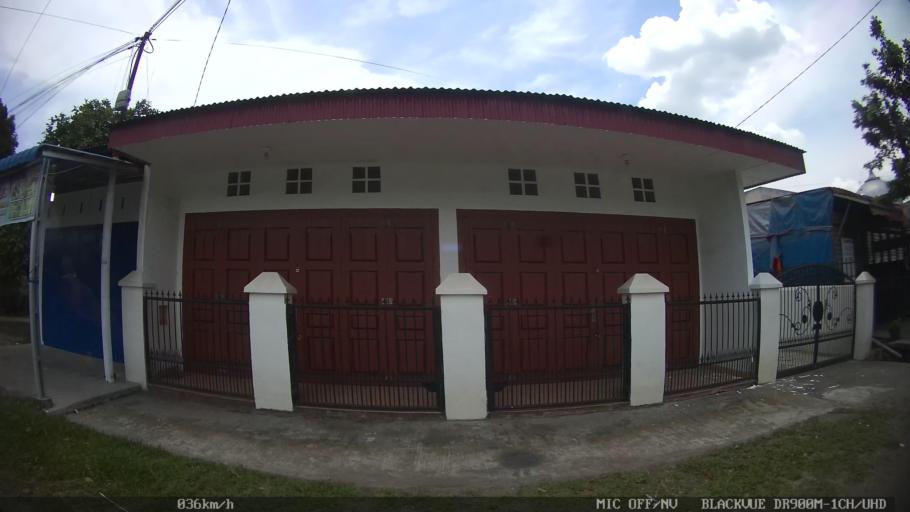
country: ID
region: North Sumatra
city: Binjai
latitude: 3.6169
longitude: 98.5183
